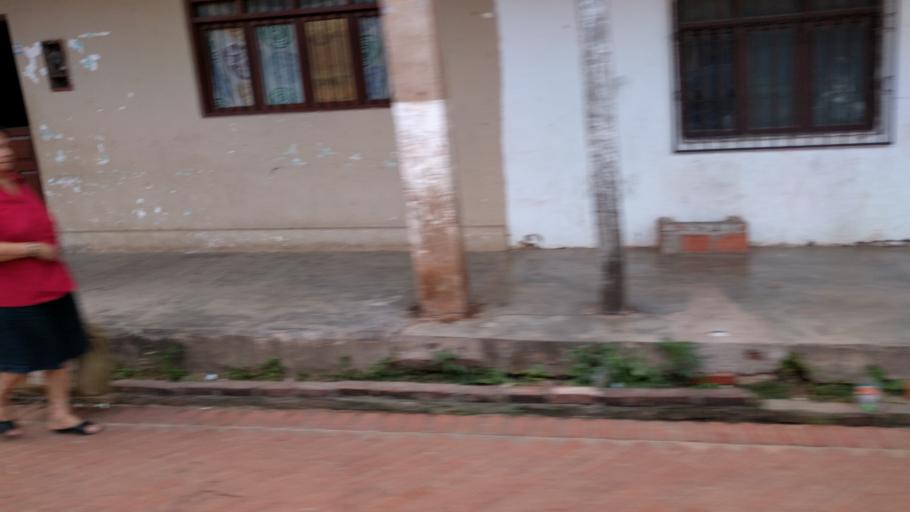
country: BO
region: Santa Cruz
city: Buena Vista
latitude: -17.4592
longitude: -63.6603
